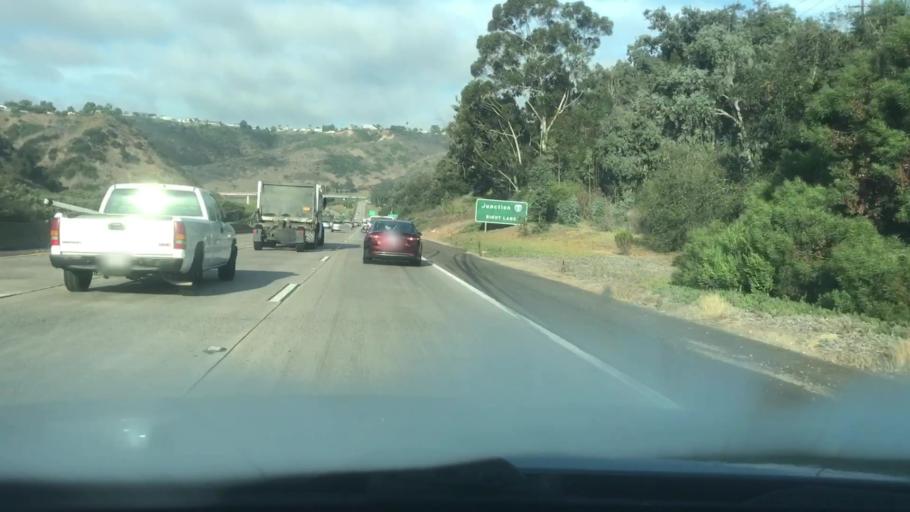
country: US
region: California
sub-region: San Diego County
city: La Jolla
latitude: 32.8372
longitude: -117.2213
